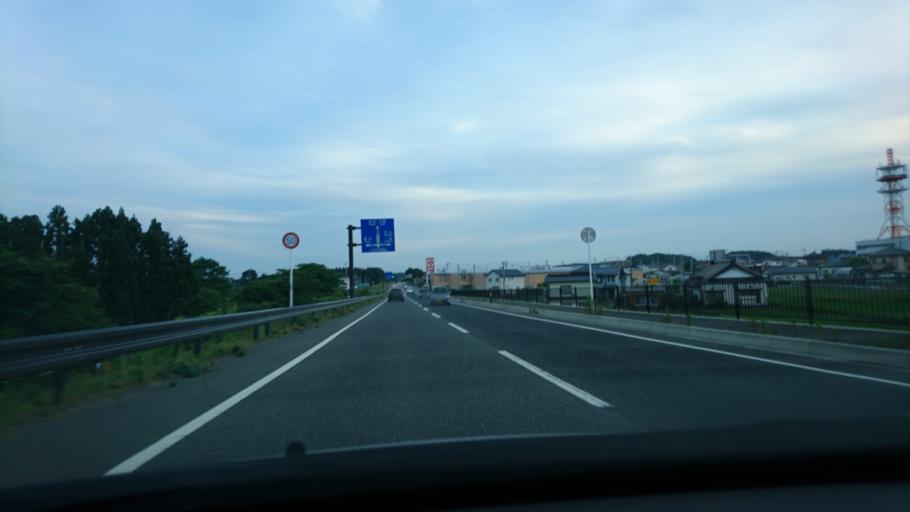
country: JP
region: Miyagi
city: Furukawa
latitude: 38.7364
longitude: 141.0370
